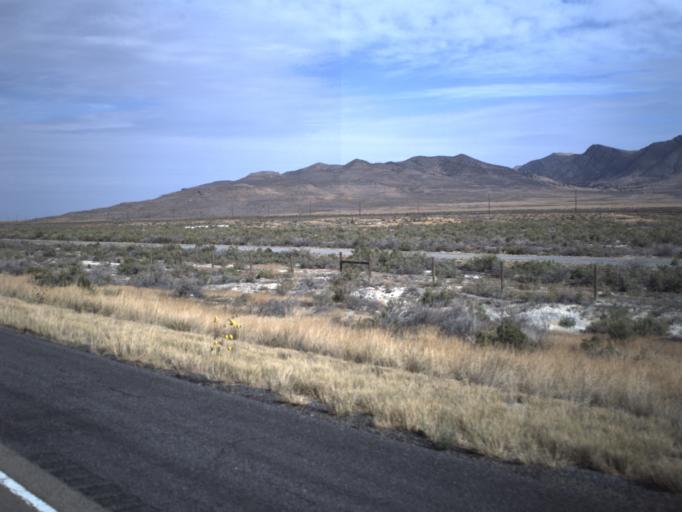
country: US
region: Utah
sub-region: Tooele County
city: Grantsville
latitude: 40.7768
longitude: -112.8066
